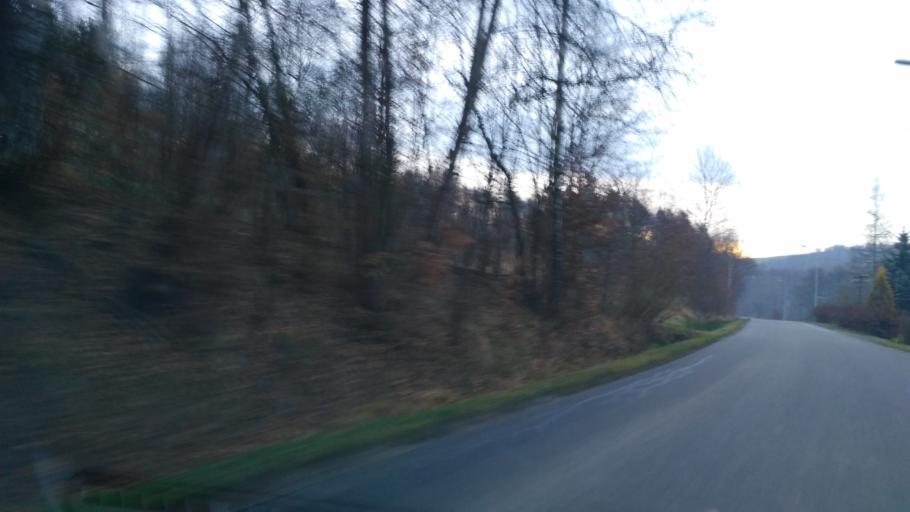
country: PL
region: Subcarpathian Voivodeship
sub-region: Powiat strzyzowski
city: Niebylec
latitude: 49.8600
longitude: 21.8934
